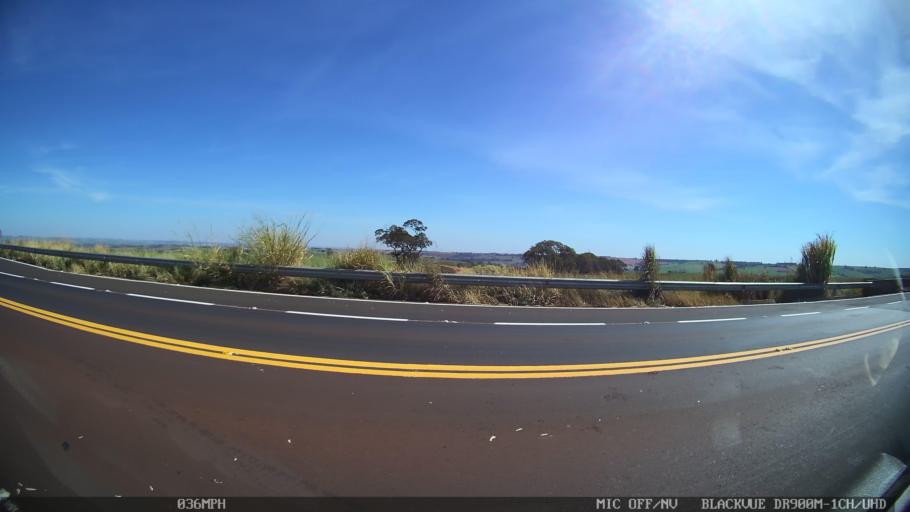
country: BR
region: Sao Paulo
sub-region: Nuporanga
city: Nuporanga
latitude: -20.5610
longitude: -47.6251
